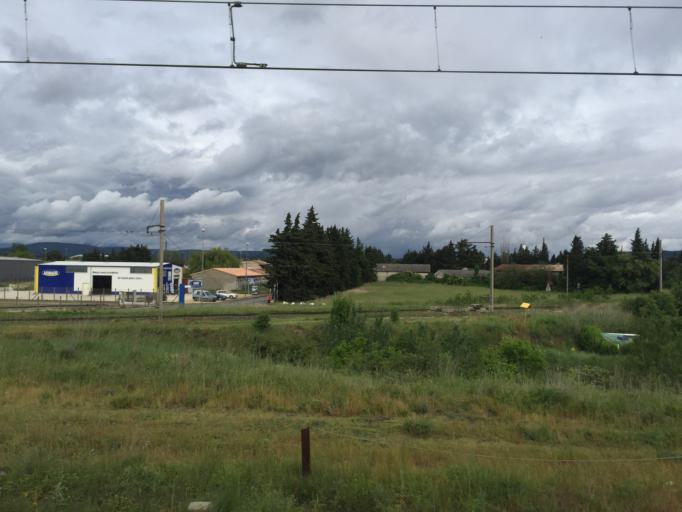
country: FR
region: Rhone-Alpes
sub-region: Departement de la Drome
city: Pierrelatte
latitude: 44.3685
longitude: 4.7031
